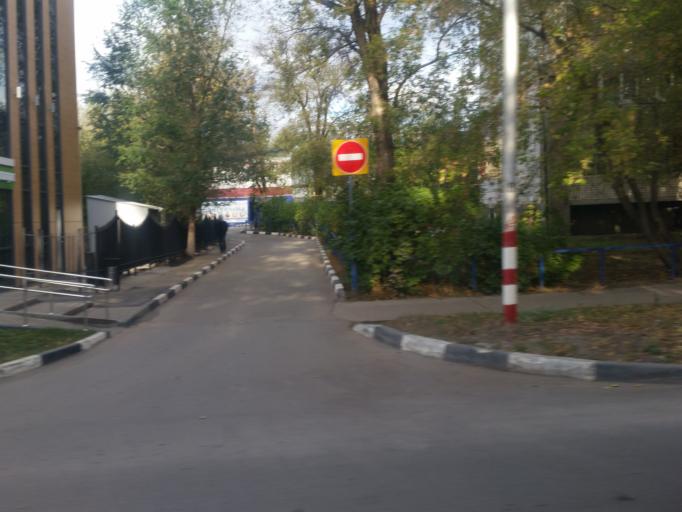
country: RU
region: Ulyanovsk
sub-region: Ulyanovskiy Rayon
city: Ulyanovsk
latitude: 54.3222
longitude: 48.3921
